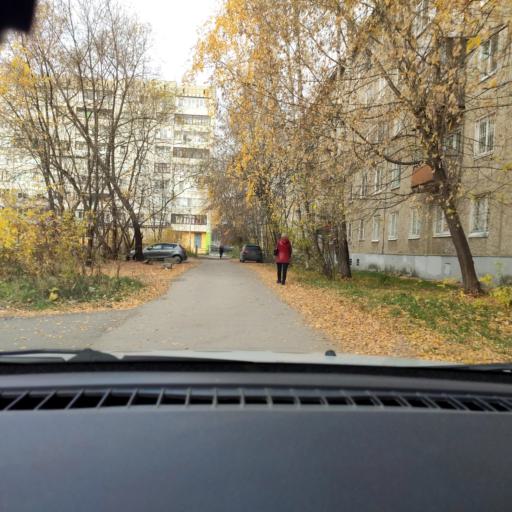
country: RU
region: Perm
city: Kondratovo
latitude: 58.0285
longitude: 56.0083
